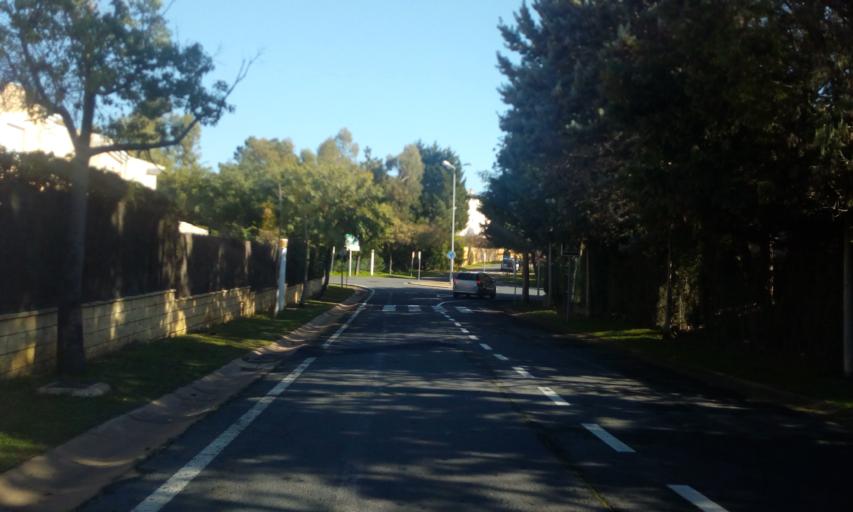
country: ES
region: Andalusia
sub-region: Provincia de Huelva
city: Lepe
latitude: 37.2101
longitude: -7.2393
